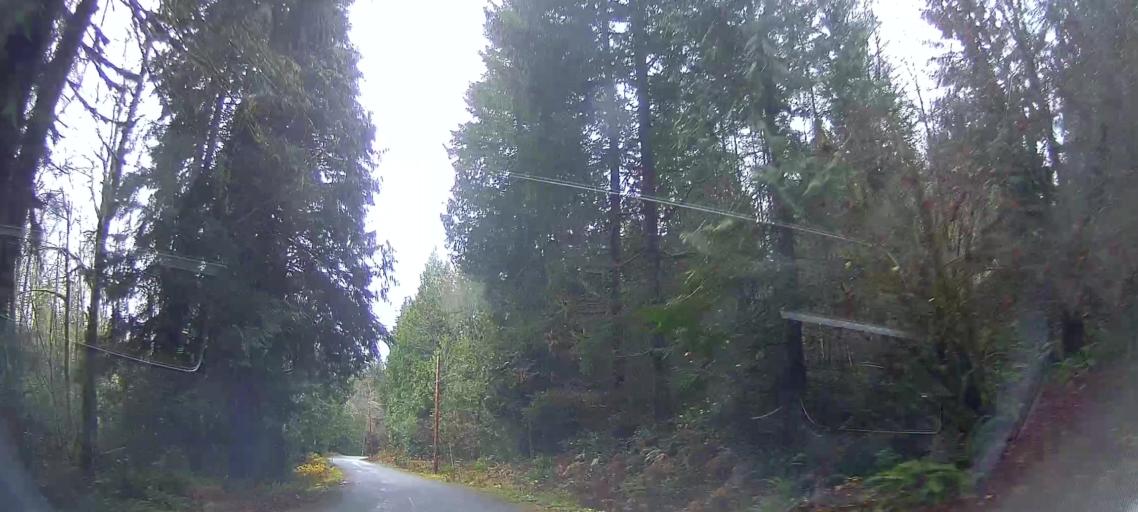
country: US
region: Washington
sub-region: Snohomish County
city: Darrington
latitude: 48.5301
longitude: -121.3962
